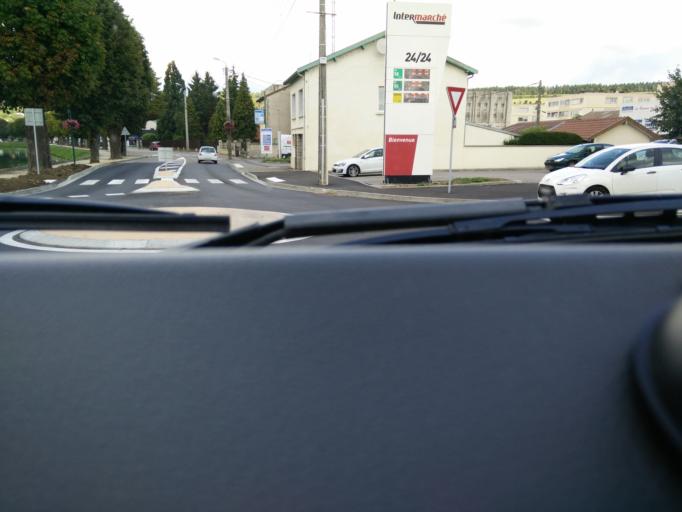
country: FR
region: Lorraine
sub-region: Departement de la Meuse
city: Verdun
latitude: 49.1685
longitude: 5.3866
